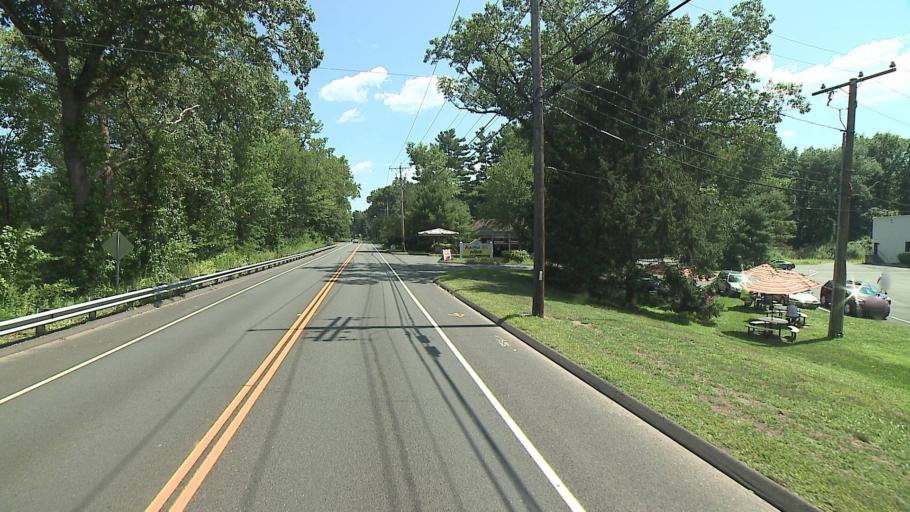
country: US
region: Connecticut
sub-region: Hartford County
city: Farmington
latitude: 41.7429
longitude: -72.8586
